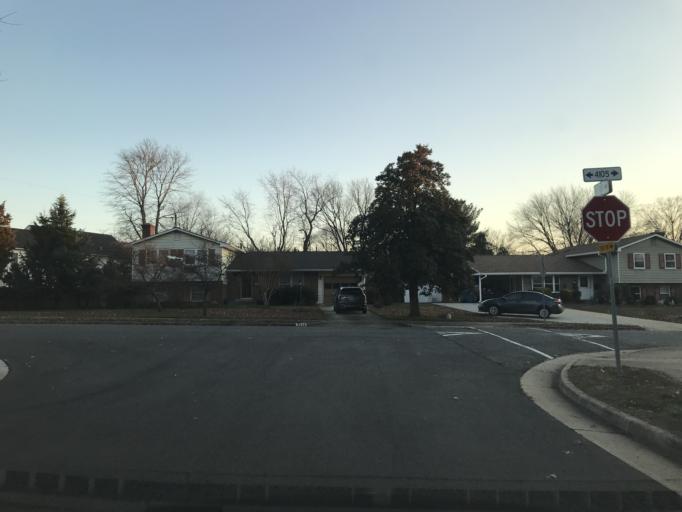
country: US
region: Virginia
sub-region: Fairfax County
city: Franconia
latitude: 38.7848
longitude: -77.1591
